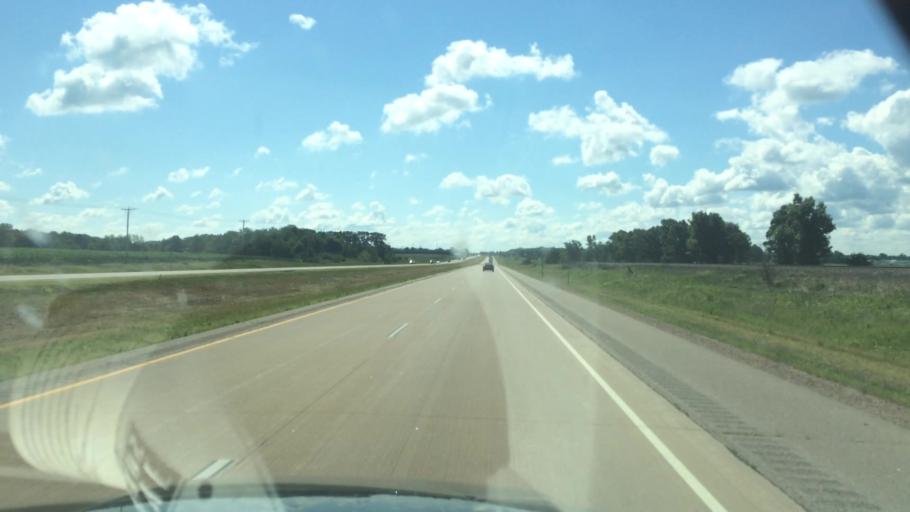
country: US
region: Wisconsin
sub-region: Portage County
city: Amherst
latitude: 44.4909
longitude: -89.3600
